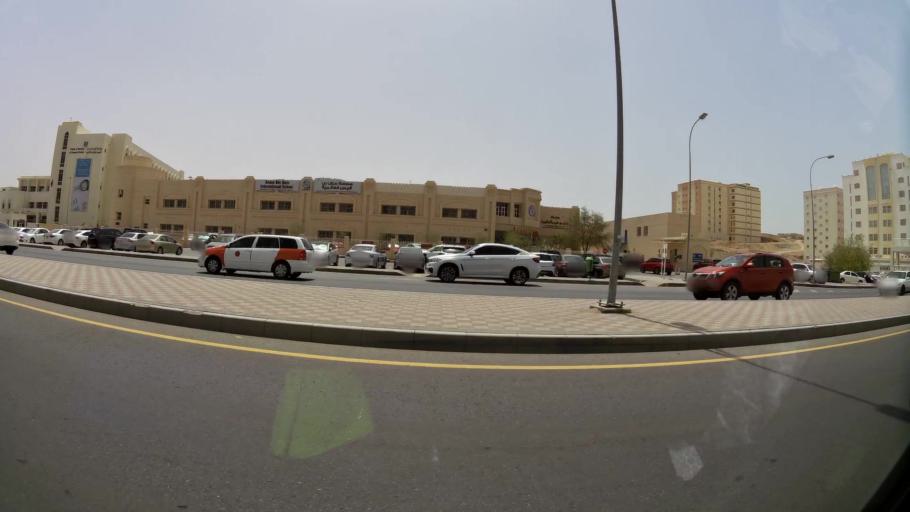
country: OM
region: Muhafazat Masqat
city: Bawshar
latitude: 23.5544
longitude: 58.4008
